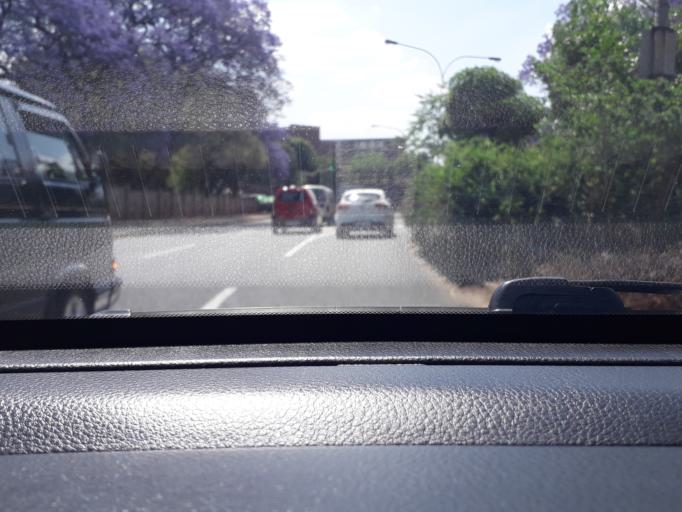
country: ZA
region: Gauteng
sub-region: City of Johannesburg Metropolitan Municipality
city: Johannesburg
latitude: -26.1795
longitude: 28.0376
